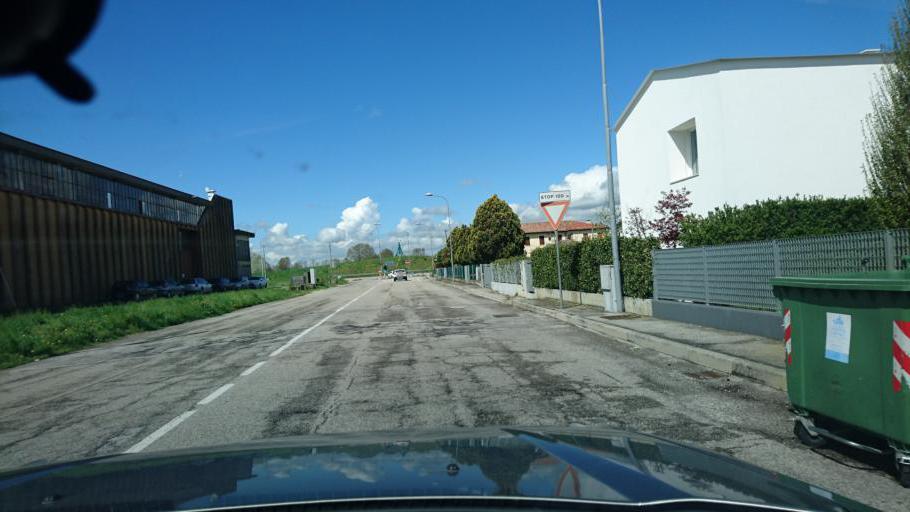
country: IT
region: Veneto
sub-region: Provincia di Padova
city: Mejaniga
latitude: 45.4707
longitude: 11.8971
